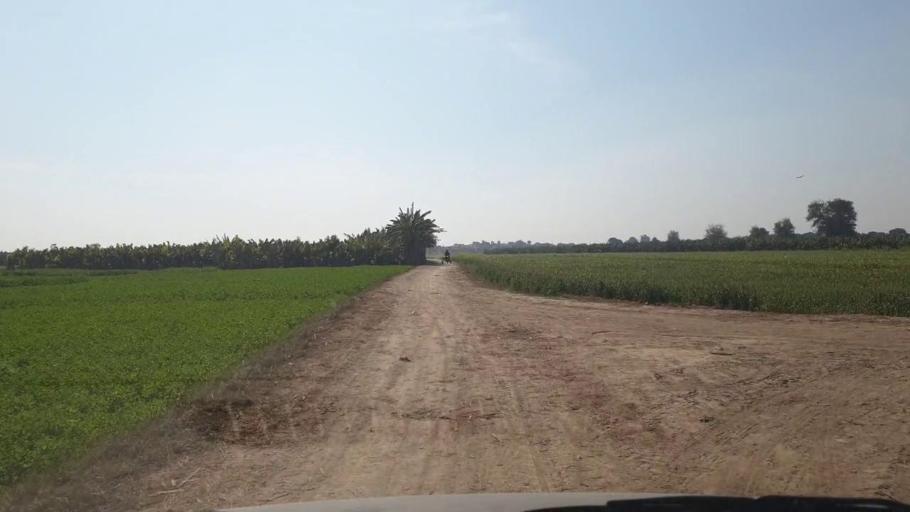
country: PK
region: Sindh
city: Tando Allahyar
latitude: 25.3950
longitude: 68.7816
